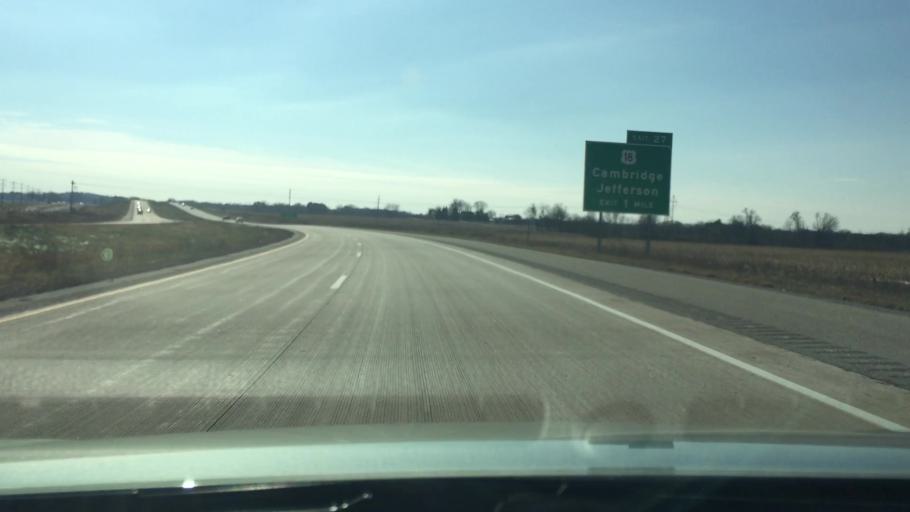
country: US
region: Wisconsin
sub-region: Jefferson County
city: Jefferson
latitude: 43.0246
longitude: -88.8276
